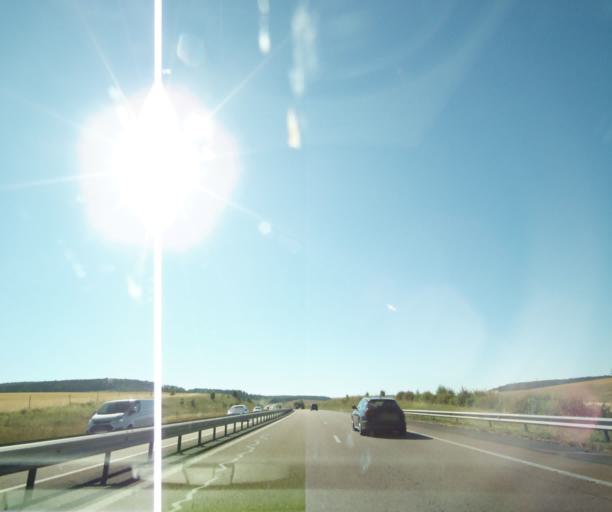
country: FR
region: Champagne-Ardenne
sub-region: Departement de l'Aube
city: Ville-sous-la-Ferte
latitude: 48.1031
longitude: 4.8013
